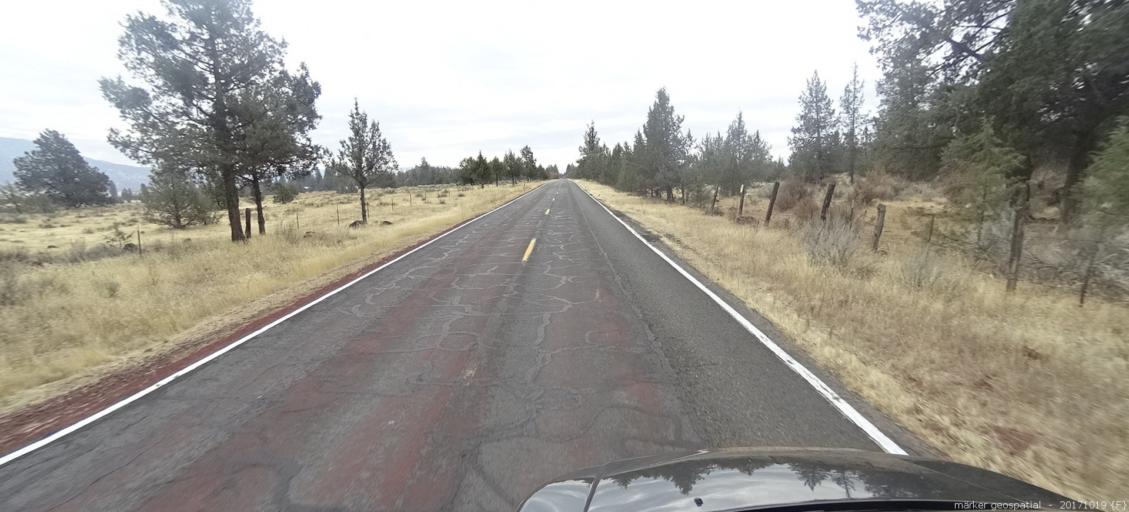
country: US
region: California
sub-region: Shasta County
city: Burney
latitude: 41.1018
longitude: -121.3240
